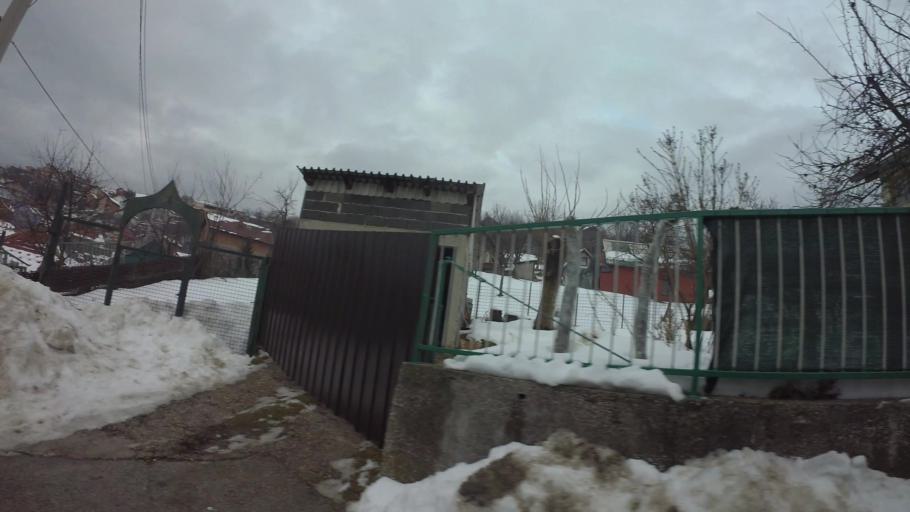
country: BA
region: Federation of Bosnia and Herzegovina
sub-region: Kanton Sarajevo
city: Sarajevo
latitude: 43.8602
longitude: 18.3515
